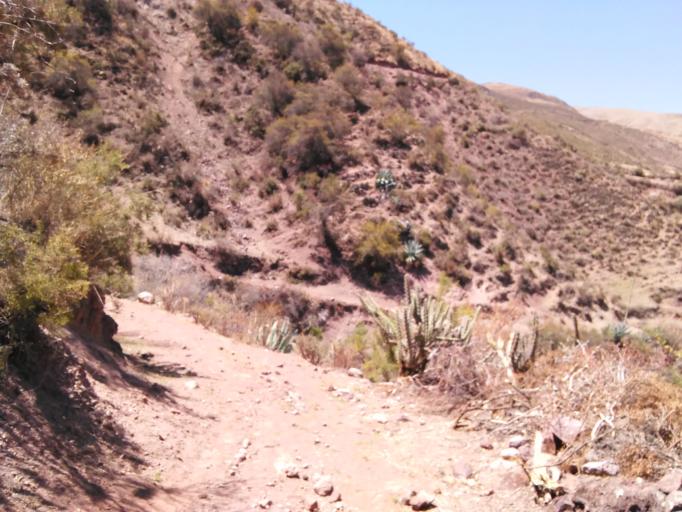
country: PE
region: Ayacucho
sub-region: Provincia de Victor Fajardo
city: Canaria
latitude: -13.8830
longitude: -73.9504
